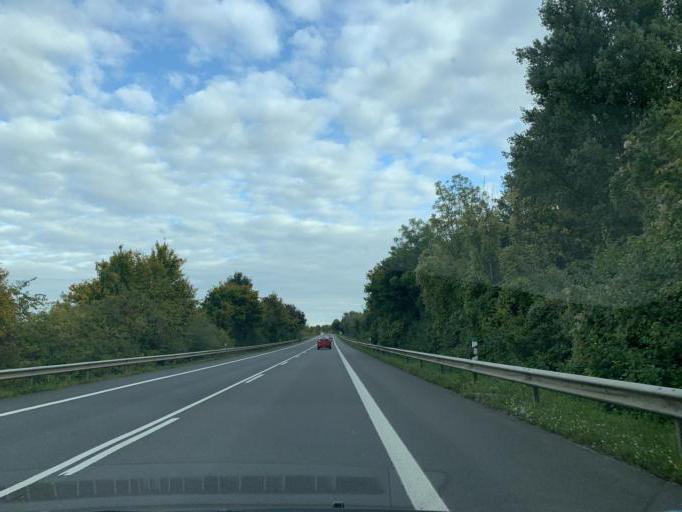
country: DE
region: North Rhine-Westphalia
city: Julich
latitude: 50.8994
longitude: 6.3731
